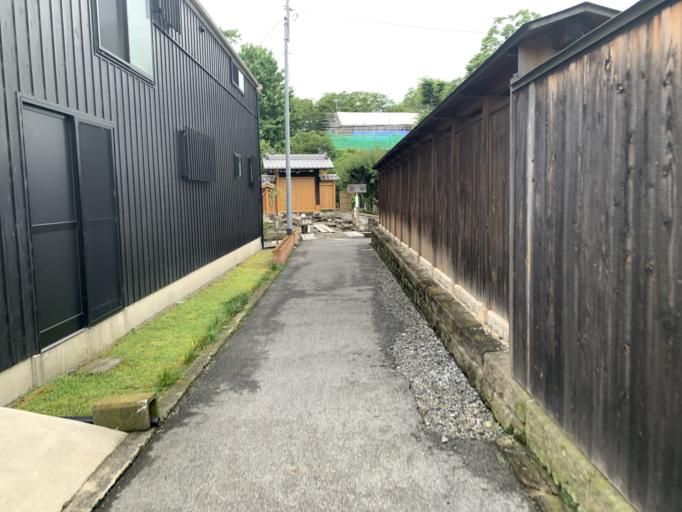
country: JP
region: Tochigi
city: Tochigi
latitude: 36.3859
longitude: 139.7329
